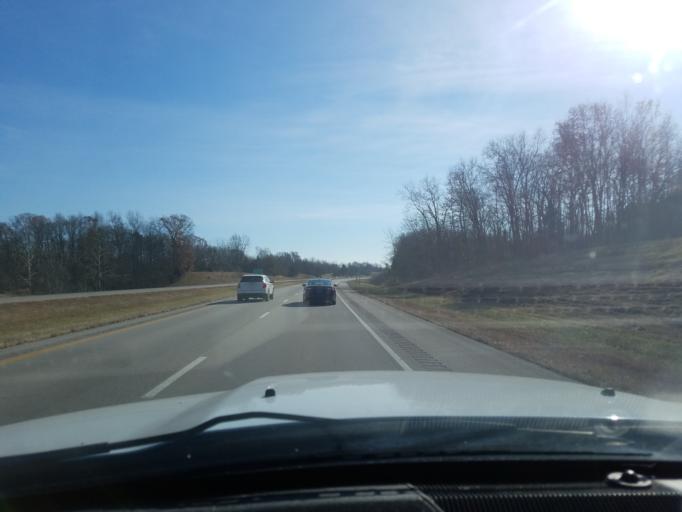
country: US
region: Ohio
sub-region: Adams County
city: Winchester
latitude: 38.9477
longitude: -83.6806
